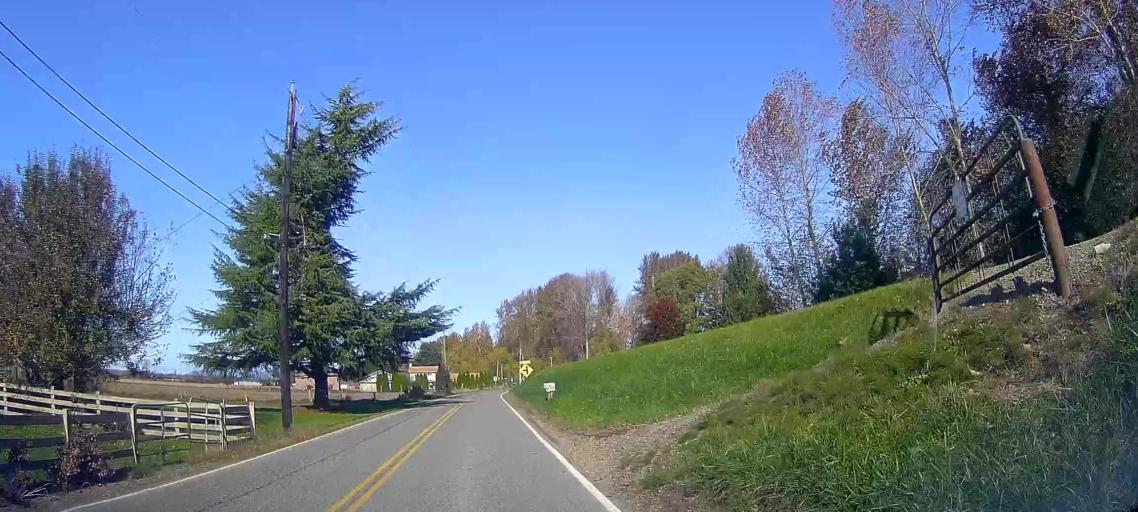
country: US
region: Washington
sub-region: Skagit County
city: Mount Vernon
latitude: 48.4046
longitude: -122.3682
